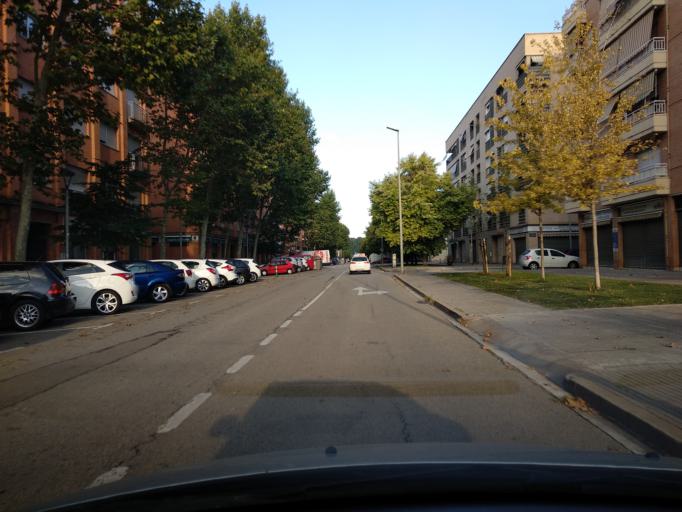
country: ES
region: Catalonia
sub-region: Provincia de Barcelona
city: Granollers
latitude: 41.5976
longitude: 2.2896
